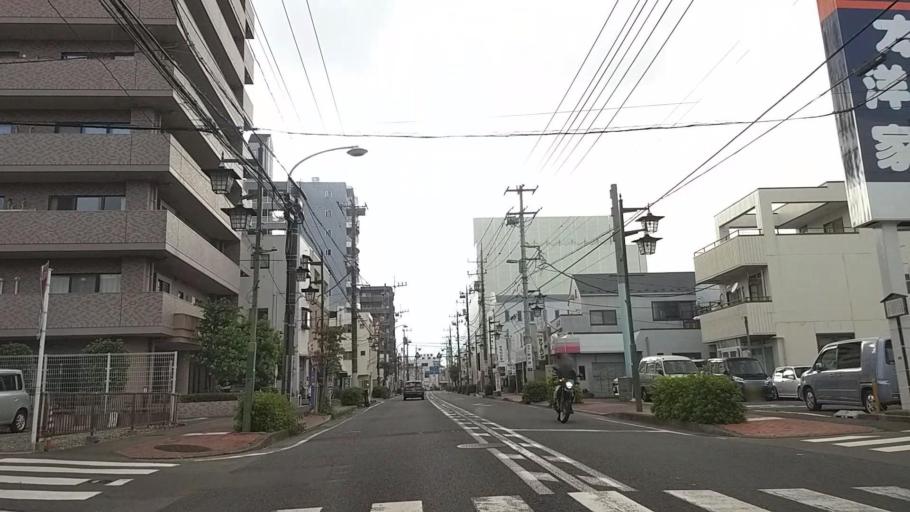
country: JP
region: Kanagawa
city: Isehara
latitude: 35.3979
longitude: 139.3077
